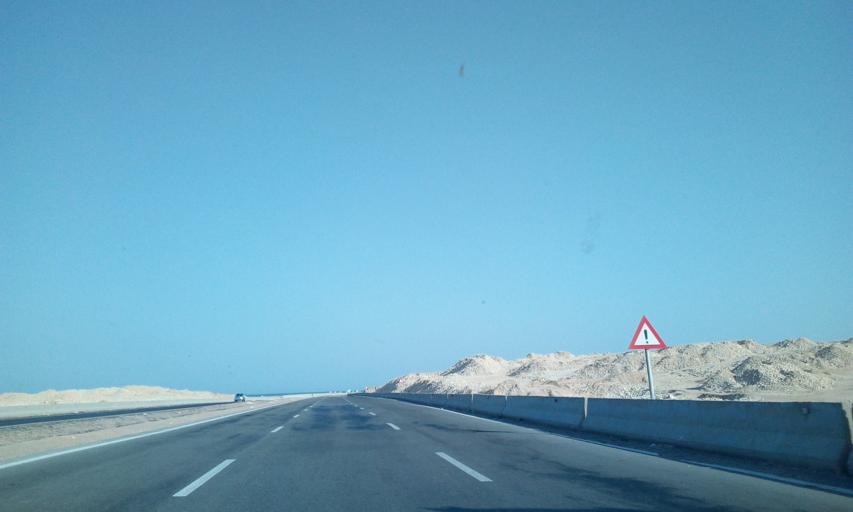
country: EG
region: As Suways
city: Ain Sukhna
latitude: 29.0965
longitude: 32.6284
